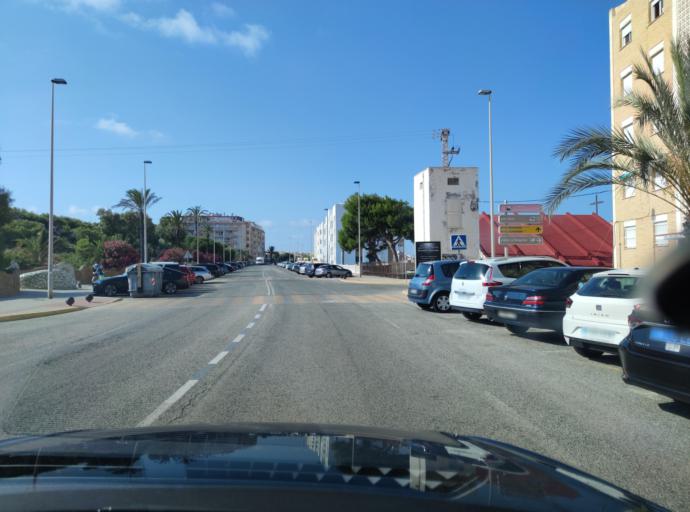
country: ES
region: Valencia
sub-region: Provincia de Alicante
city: Guardamar del Segura
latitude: 38.0776
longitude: -0.6502
